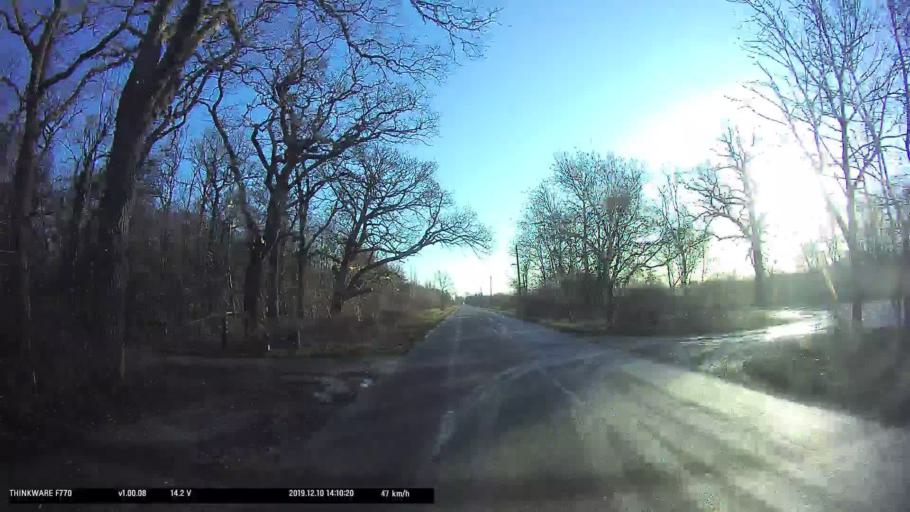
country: DK
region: Capital Region
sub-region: Tarnby Kommune
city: Tarnby
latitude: 55.5723
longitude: 12.5811
